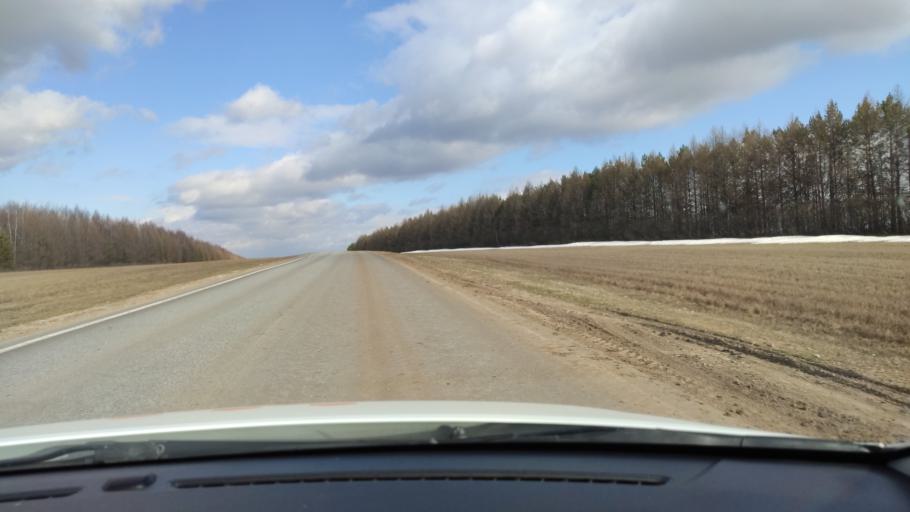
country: RU
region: Tatarstan
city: Vysokaya Gora
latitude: 56.2245
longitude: 49.2874
